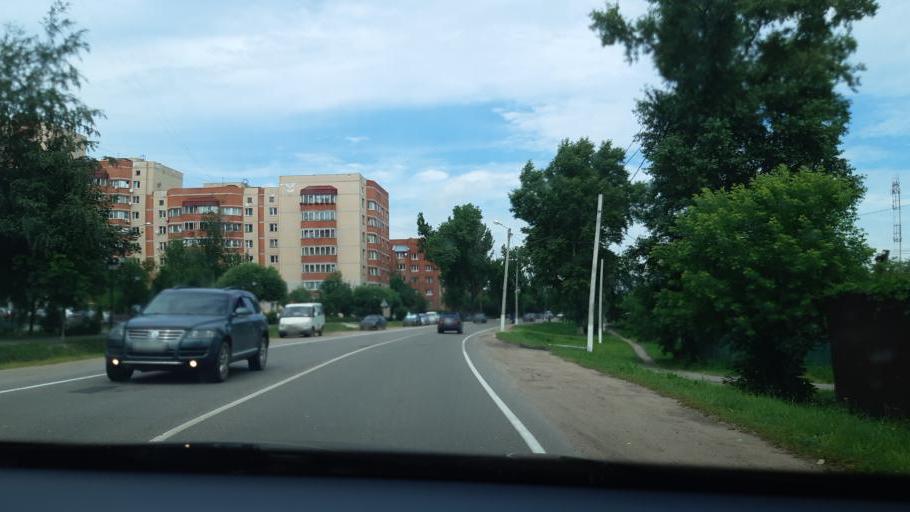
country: RU
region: Moskovskaya
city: Bol'shiye Vyazemy
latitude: 55.6244
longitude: 36.9833
